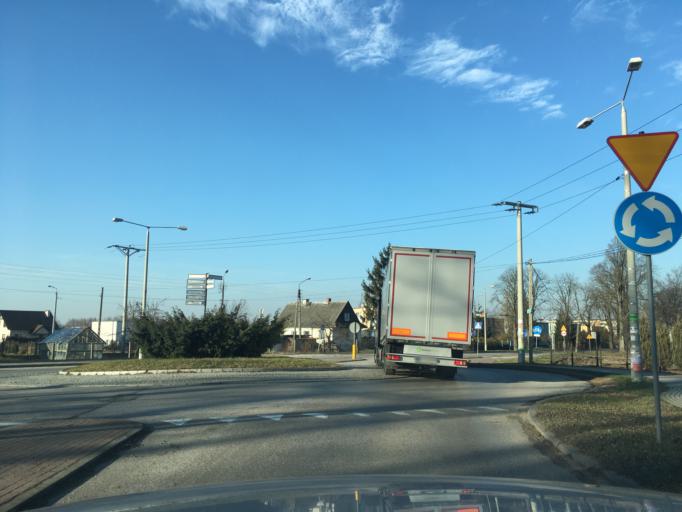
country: PL
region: Masovian Voivodeship
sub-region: Powiat pruszkowski
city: Nadarzyn
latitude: 52.0497
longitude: 20.7829
